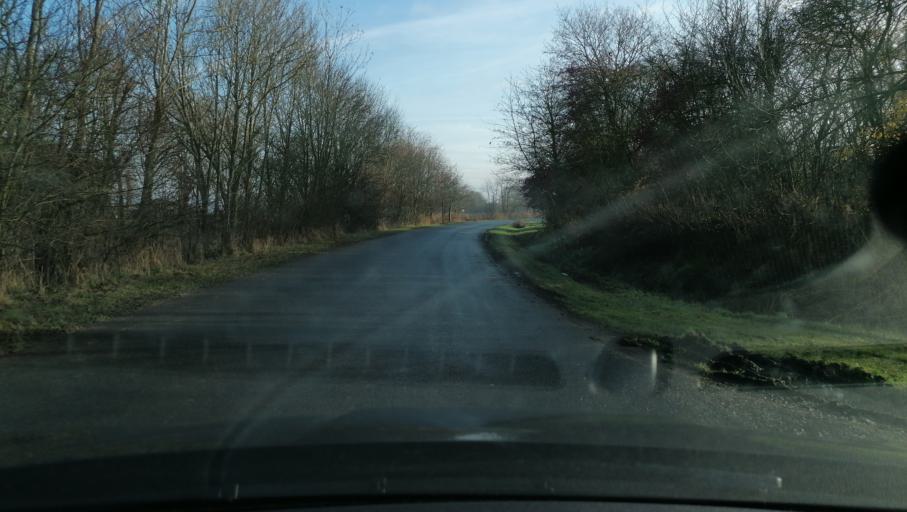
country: DE
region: Schleswig-Holstein
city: Epenwohrden
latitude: 54.1076
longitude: 9.0325
